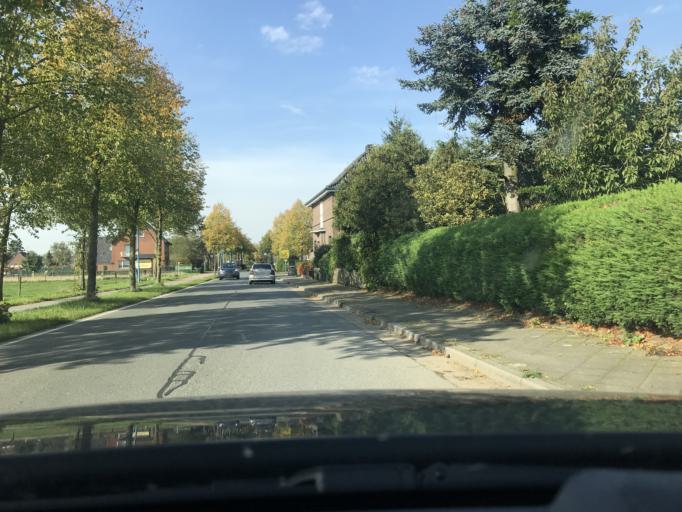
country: DE
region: North Rhine-Westphalia
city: Kalkar
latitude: 51.7619
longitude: 6.2593
